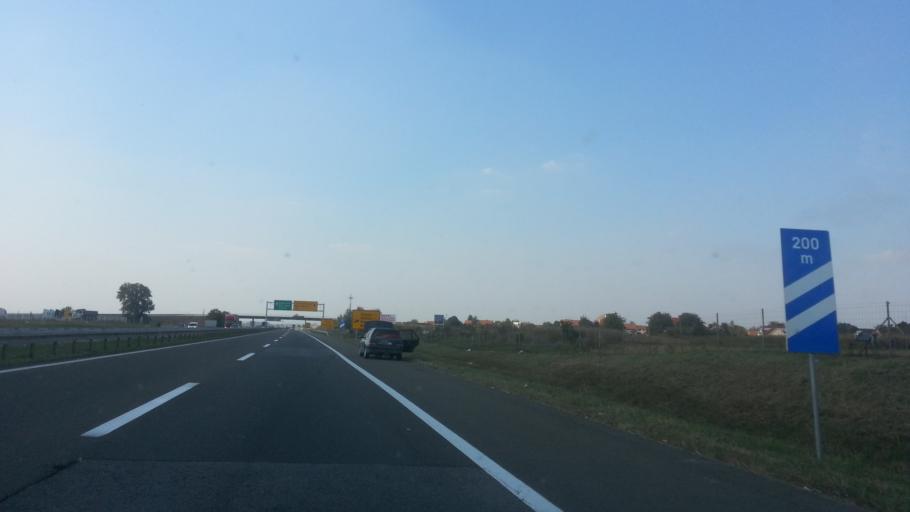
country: RS
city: Novi Banovci
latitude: 44.9410
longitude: 20.2862
